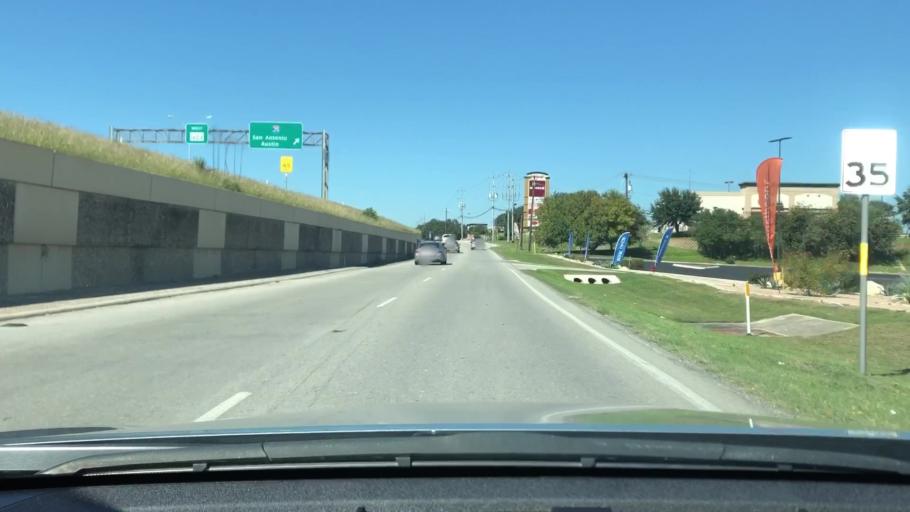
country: US
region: Texas
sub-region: Bexar County
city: Live Oak
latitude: 29.5611
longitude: -98.3270
